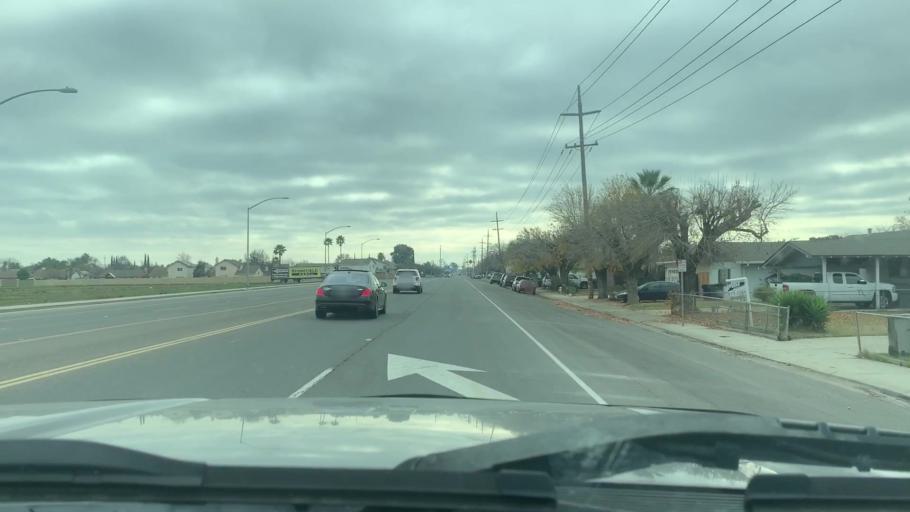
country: US
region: California
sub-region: Merced County
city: Los Banos
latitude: 37.0711
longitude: -120.8352
